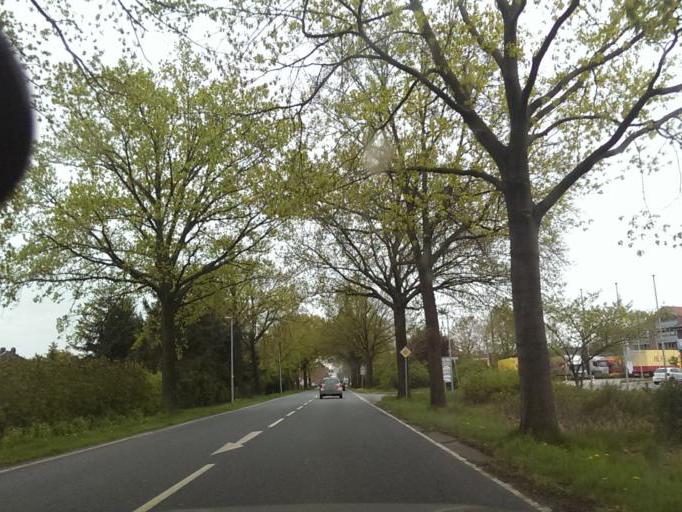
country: DE
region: Lower Saxony
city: Elze
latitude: 52.5870
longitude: 9.7285
